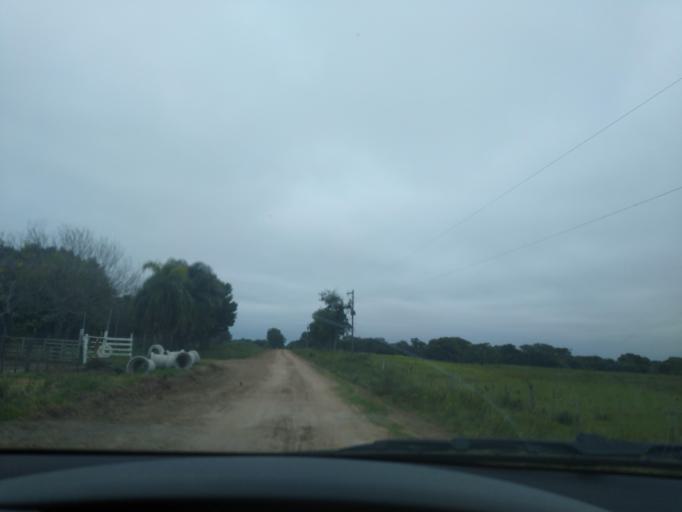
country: AR
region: Chaco
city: Colonia Benitez
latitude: -27.3604
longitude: -58.9593
